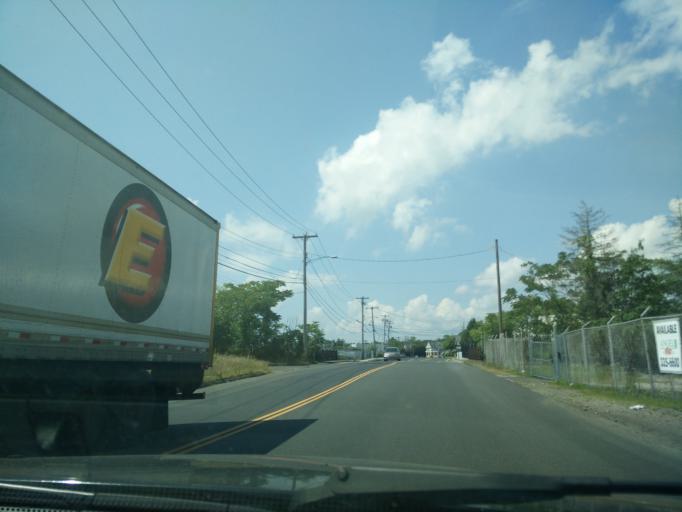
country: US
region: Connecticut
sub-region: Fairfield County
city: Bridgeport
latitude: 41.1675
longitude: -73.2230
